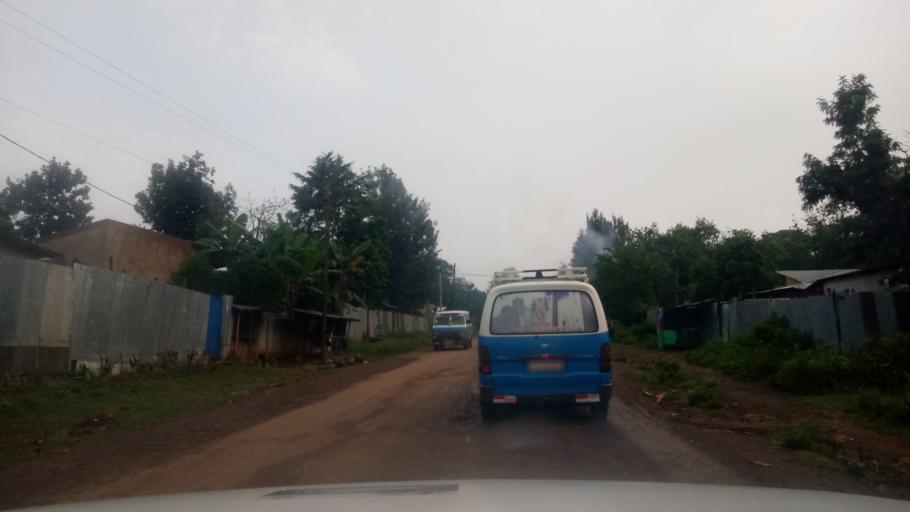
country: ET
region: Oromiya
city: Jima
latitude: 7.6956
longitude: 36.8172
